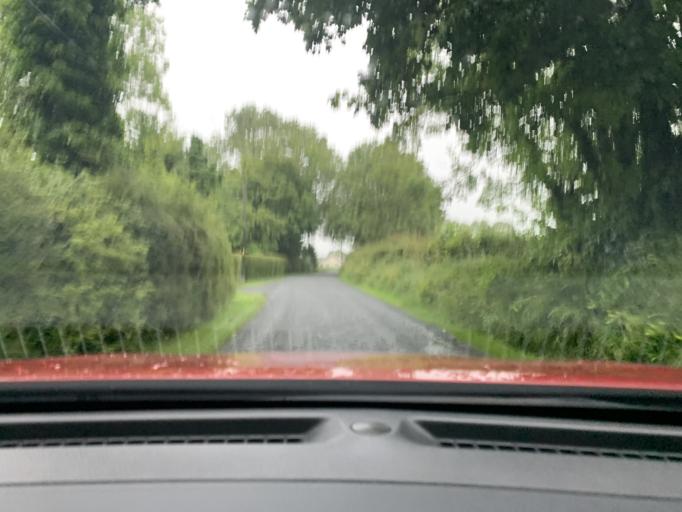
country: IE
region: Connaught
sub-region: Sligo
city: Sligo
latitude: 54.3191
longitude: -8.4556
